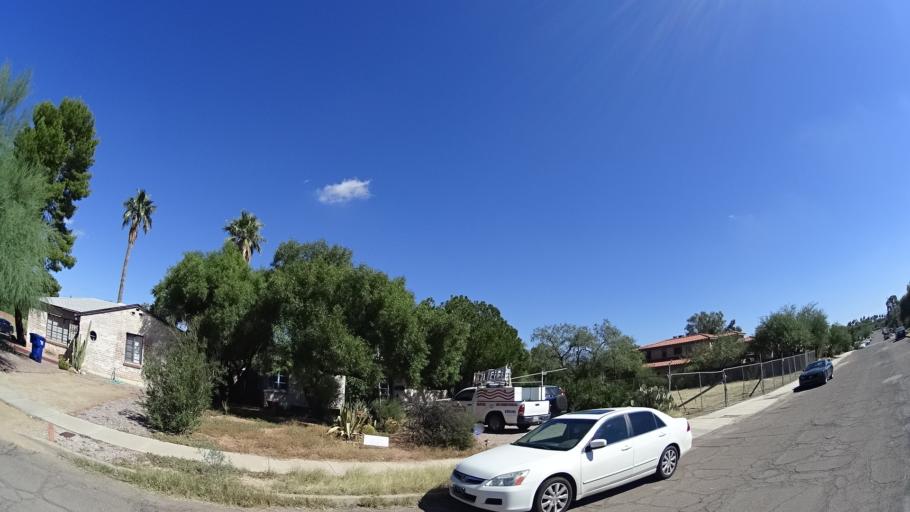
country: US
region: Arizona
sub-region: Pima County
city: Tucson
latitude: 32.2478
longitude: -110.9481
